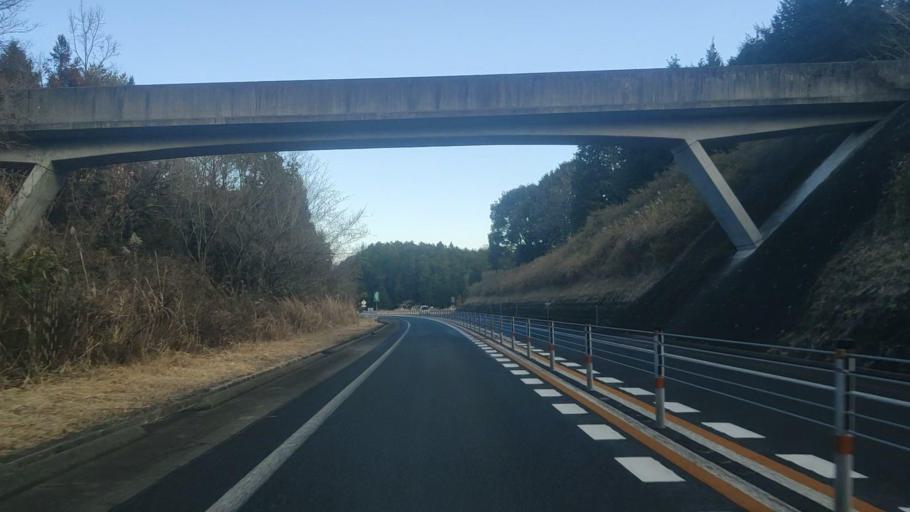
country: JP
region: Oita
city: Hiji
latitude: 33.4024
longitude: 131.4298
